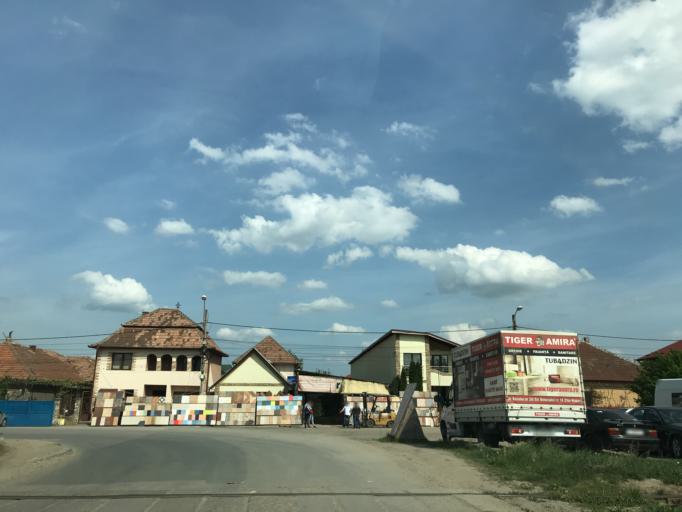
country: RO
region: Cluj
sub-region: Municipiul Cluj-Napoca
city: Cluj-Napoca
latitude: 46.7840
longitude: 23.6386
